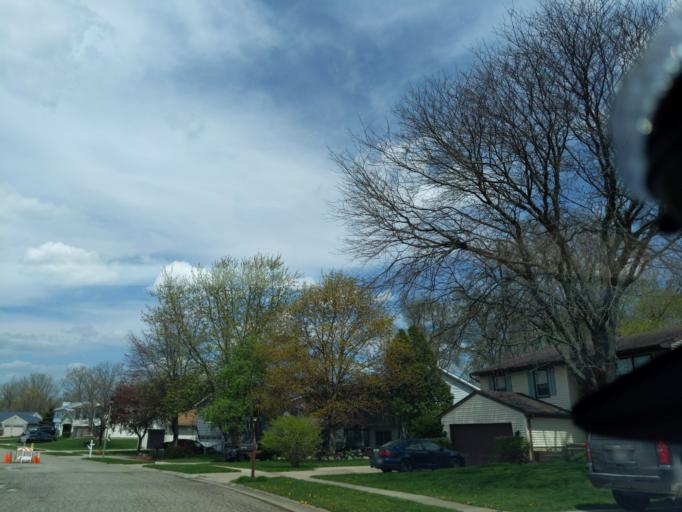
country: US
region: Michigan
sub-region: Eaton County
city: Waverly
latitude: 42.7291
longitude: -84.6174
